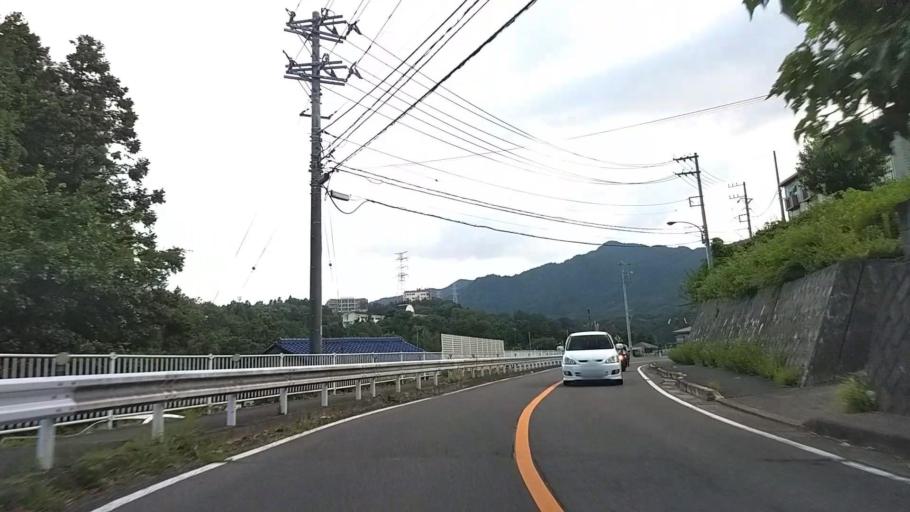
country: JP
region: Yamanashi
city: Uenohara
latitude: 35.6039
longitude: 139.2199
